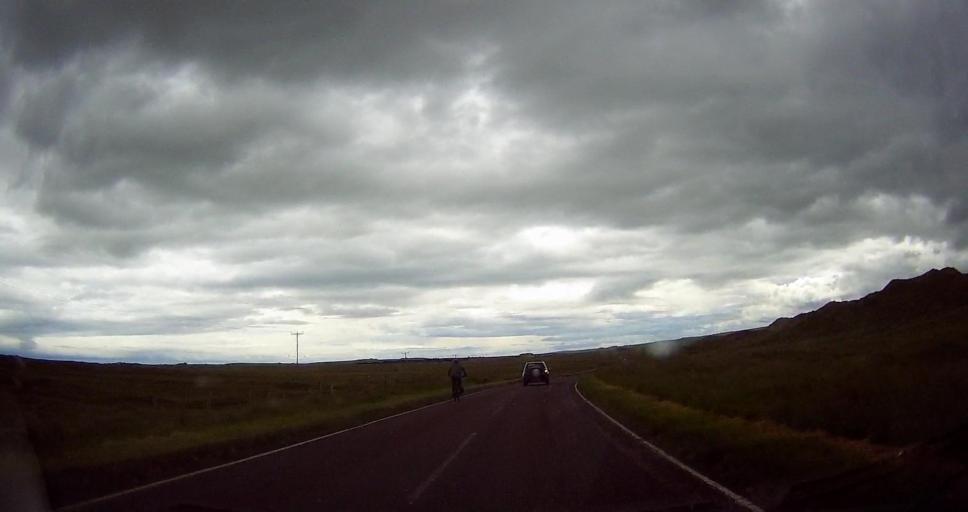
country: GB
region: Scotland
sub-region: Highland
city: Thurso
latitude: 58.6079
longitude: -3.3440
